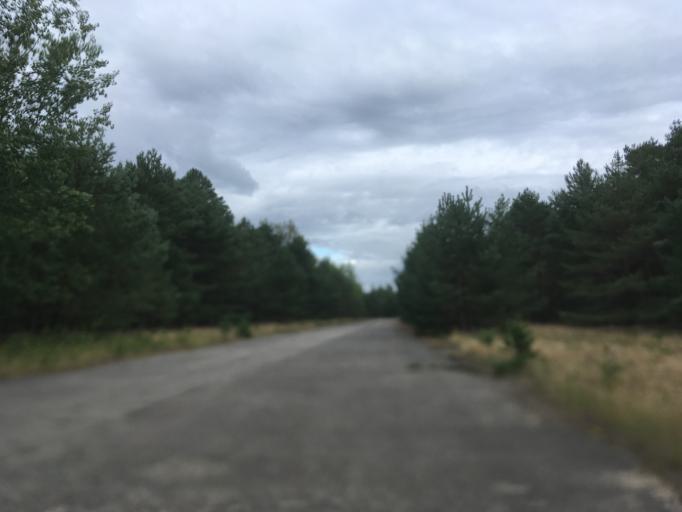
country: DE
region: Brandenburg
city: Halbe
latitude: 52.0373
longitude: 13.7627
